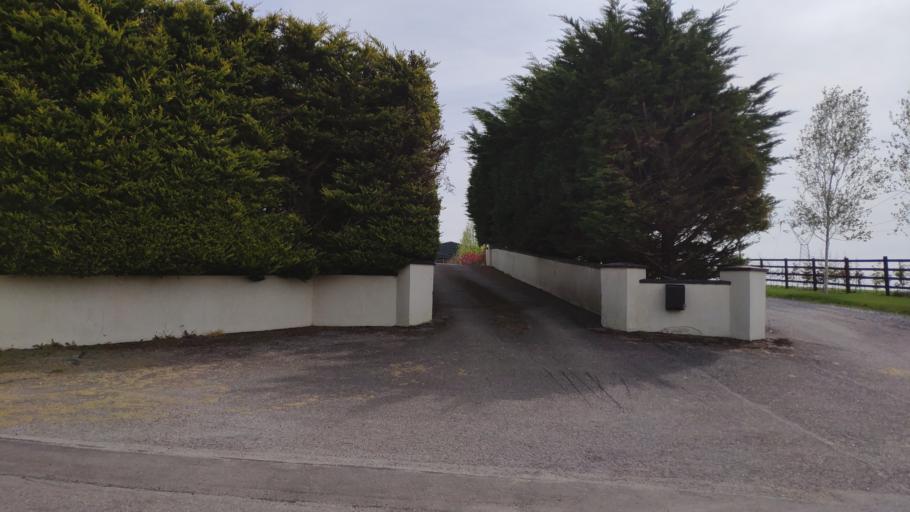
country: IE
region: Munster
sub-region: County Cork
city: Blarney
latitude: 51.9759
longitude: -8.5135
